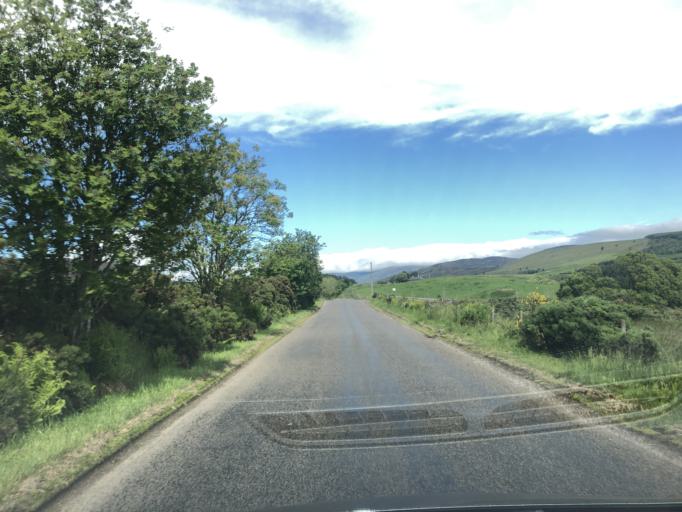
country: GB
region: Scotland
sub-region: Angus
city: Kirriemuir
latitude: 56.7514
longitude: -3.0150
